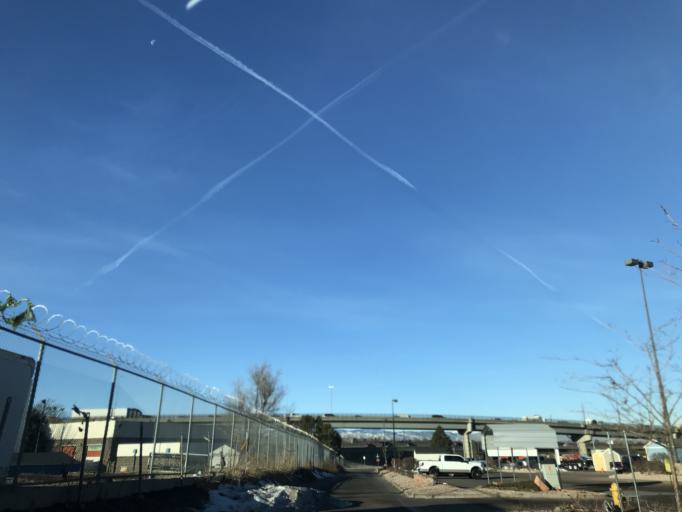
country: US
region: Colorado
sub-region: Denver County
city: Denver
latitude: 39.7058
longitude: -104.9933
